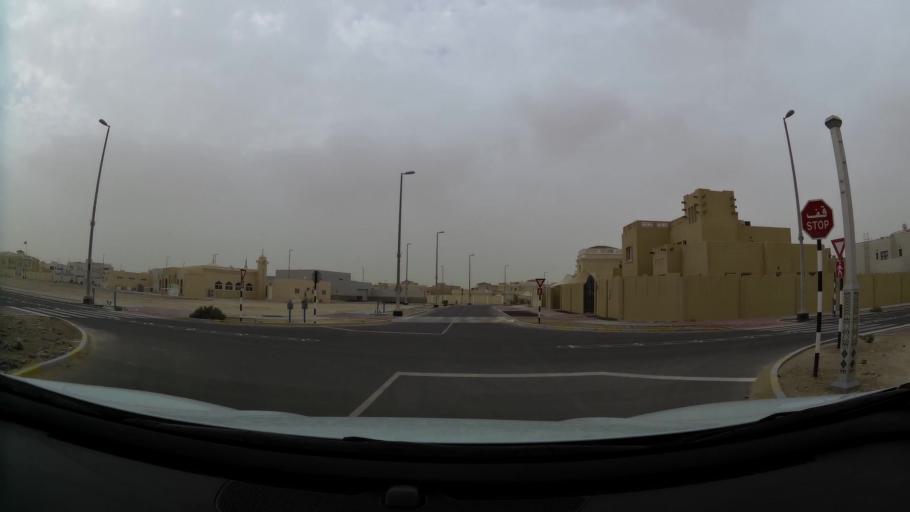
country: AE
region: Abu Dhabi
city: Abu Dhabi
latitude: 24.4533
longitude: 54.7410
